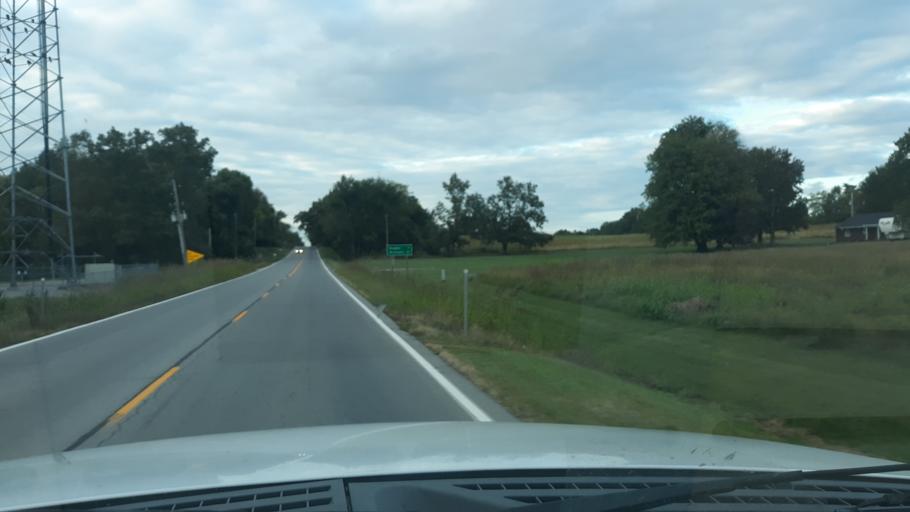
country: US
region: Illinois
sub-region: Saline County
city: Eldorado
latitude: 37.8201
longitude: -88.4523
